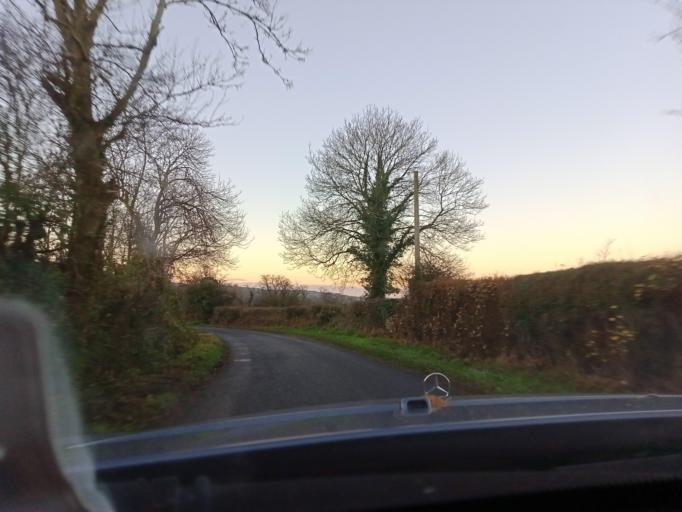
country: IE
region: Leinster
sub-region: Kilkenny
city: Thomastown
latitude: 52.4313
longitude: -7.1017
